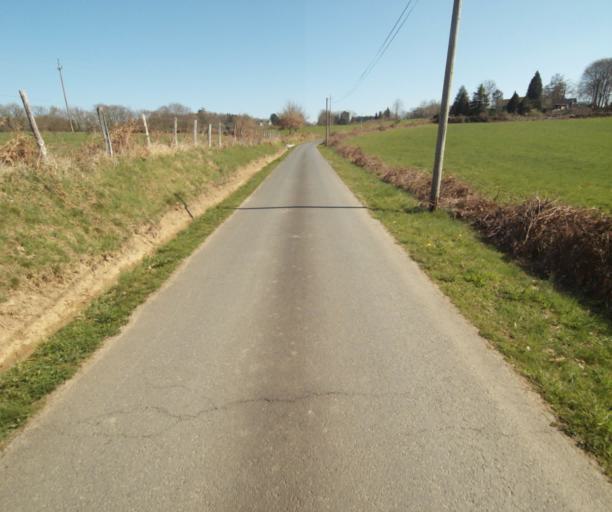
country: FR
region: Limousin
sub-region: Departement de la Correze
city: Saint-Mexant
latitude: 45.2981
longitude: 1.6104
